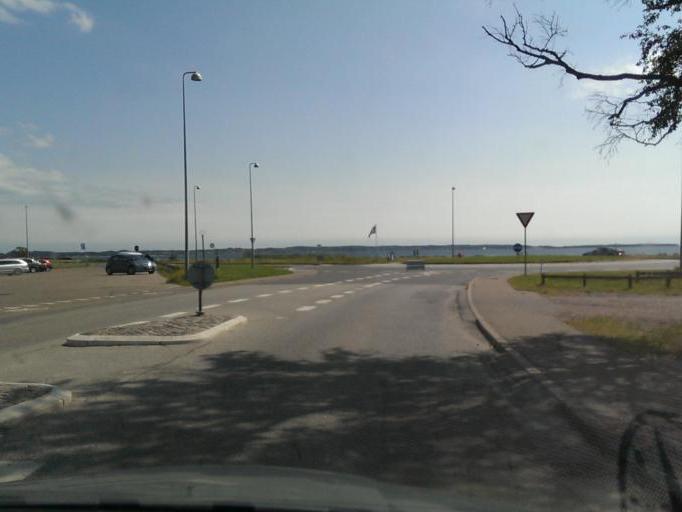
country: DK
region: Central Jutland
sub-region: Syddjurs Kommune
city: Ebeltoft
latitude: 56.2294
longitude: 10.6051
